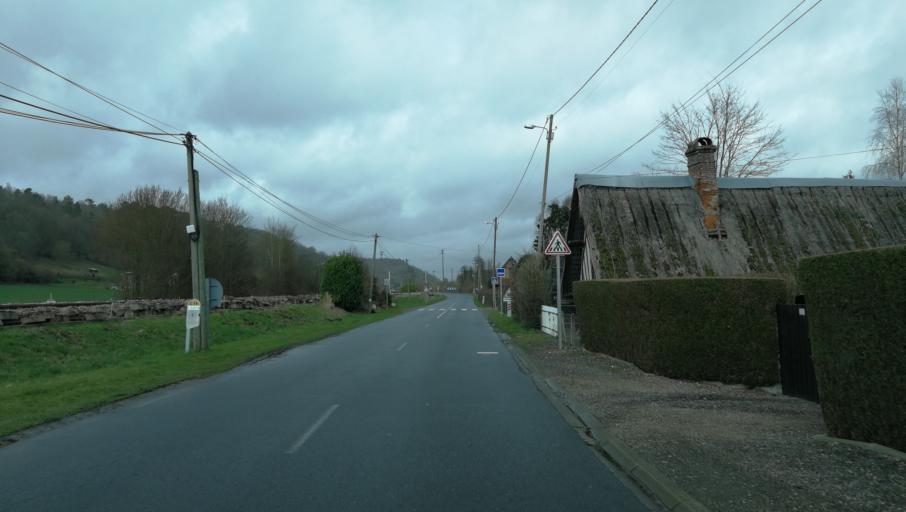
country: FR
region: Haute-Normandie
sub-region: Departement de l'Eure
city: Brionne
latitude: 49.2201
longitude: 0.6982
